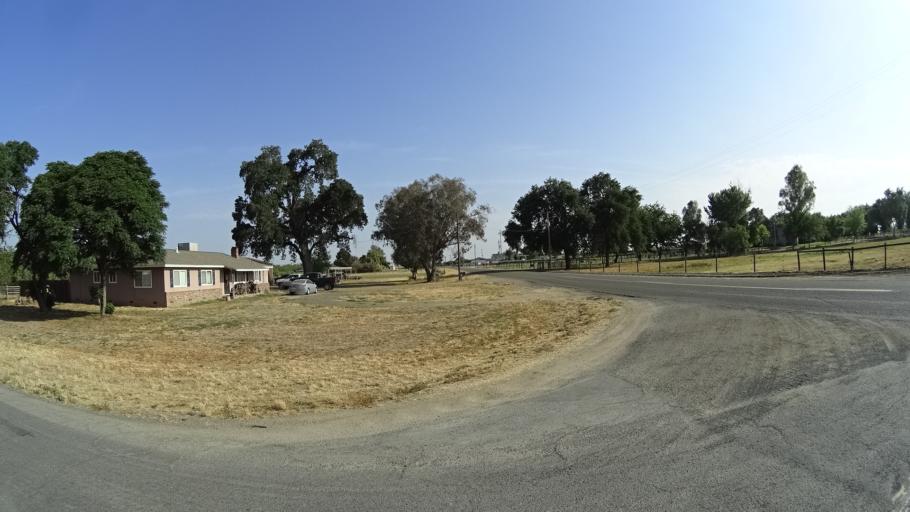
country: US
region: California
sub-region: Fresno County
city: Riverdale
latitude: 36.3586
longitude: -119.8342
